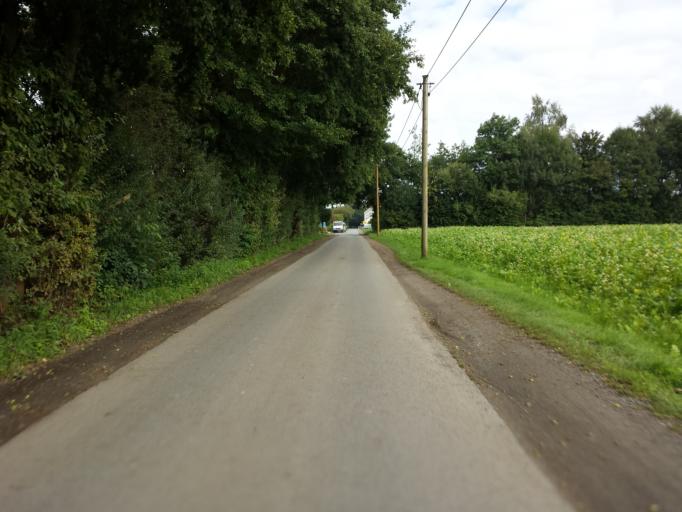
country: DE
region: North Rhine-Westphalia
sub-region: Regierungsbezirk Detmold
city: Delbruck
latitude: 51.7838
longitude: 8.4952
